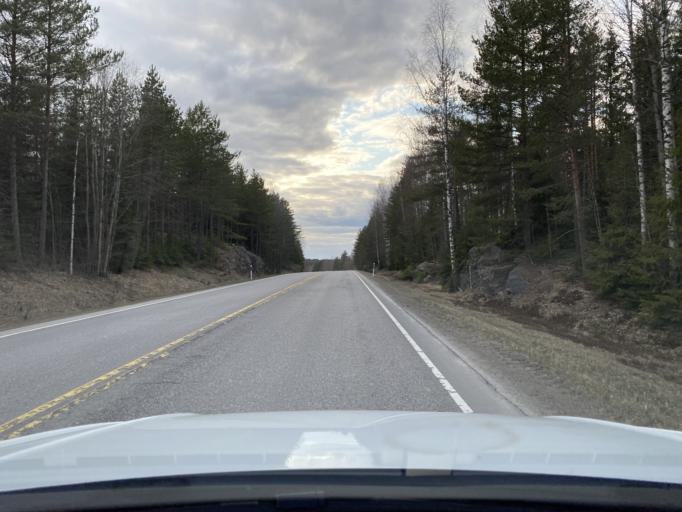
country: FI
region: Haeme
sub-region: Riihimaeki
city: Loppi
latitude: 60.7459
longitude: 24.3446
